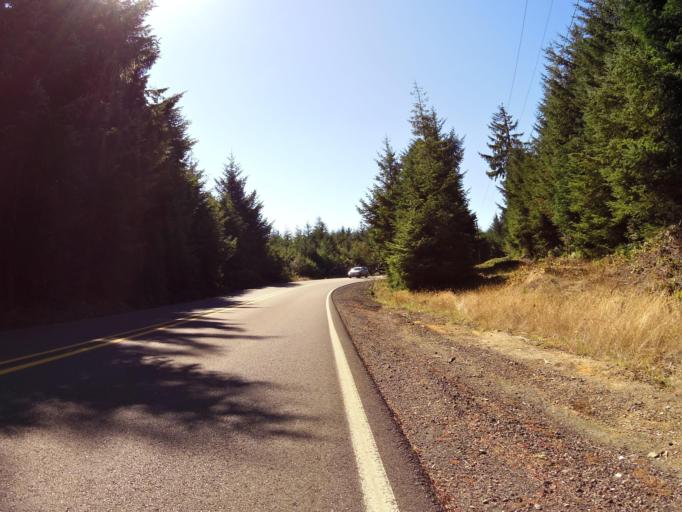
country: US
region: Oregon
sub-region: Coos County
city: Barview
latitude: 43.2794
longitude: -124.3470
